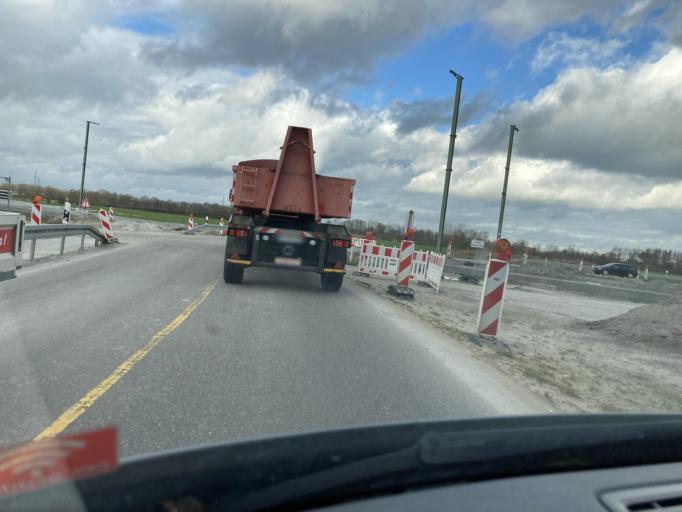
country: DE
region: Lower Saxony
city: Sande
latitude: 53.5169
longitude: 8.0226
